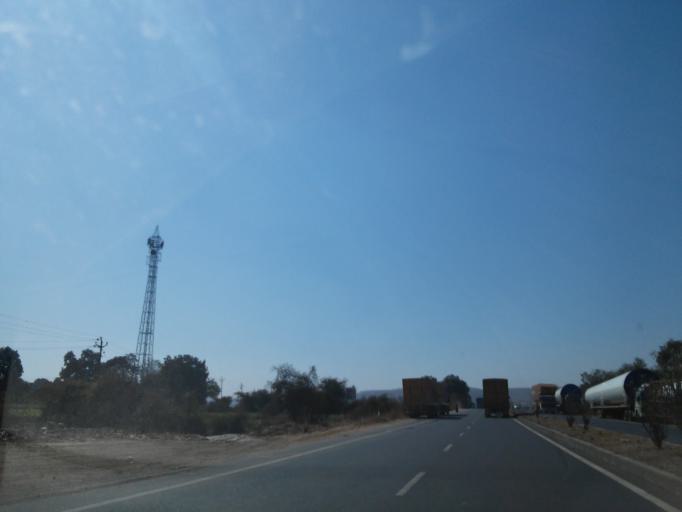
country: IN
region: Gujarat
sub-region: Sabar Kantha
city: Meghraj
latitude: 23.7239
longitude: 73.4002
